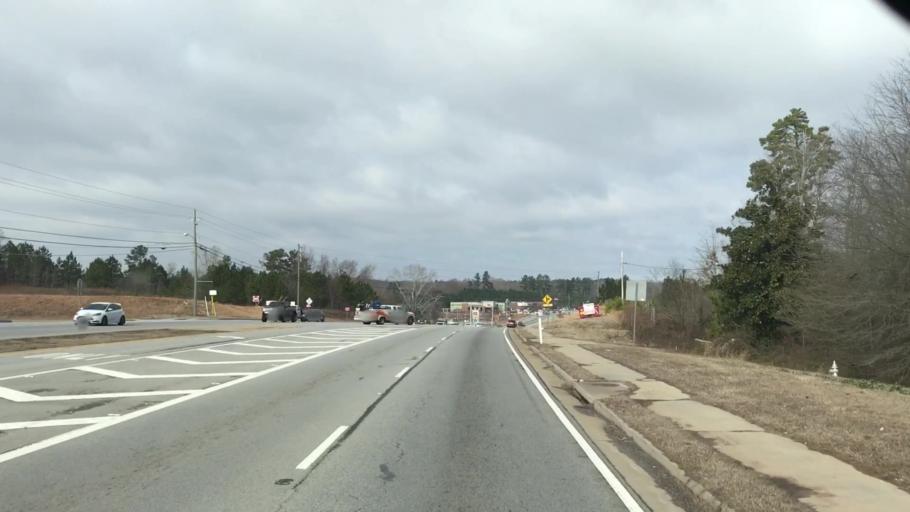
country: US
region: Georgia
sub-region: Hall County
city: Oakwood
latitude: 34.1905
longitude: -83.8571
